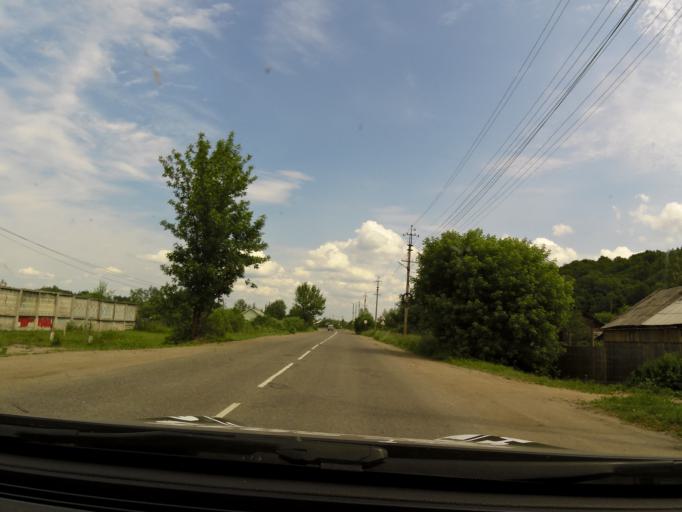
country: RU
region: Kostroma
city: Galich
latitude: 58.3971
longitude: 42.4170
